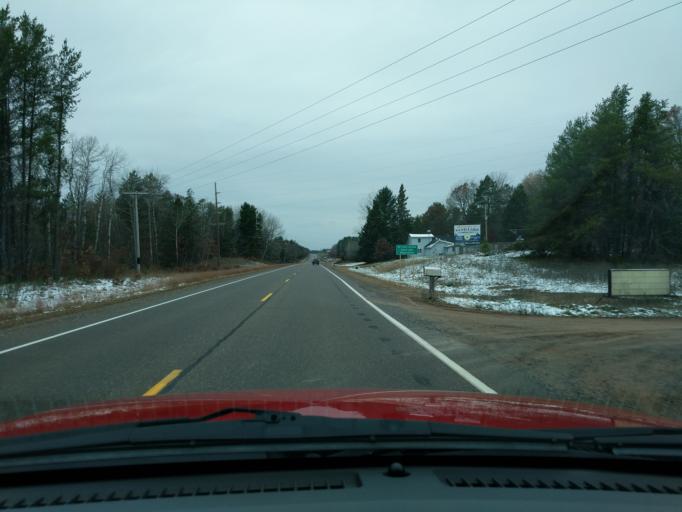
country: US
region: Wisconsin
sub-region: Burnett County
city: Siren
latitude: 45.8088
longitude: -92.1843
